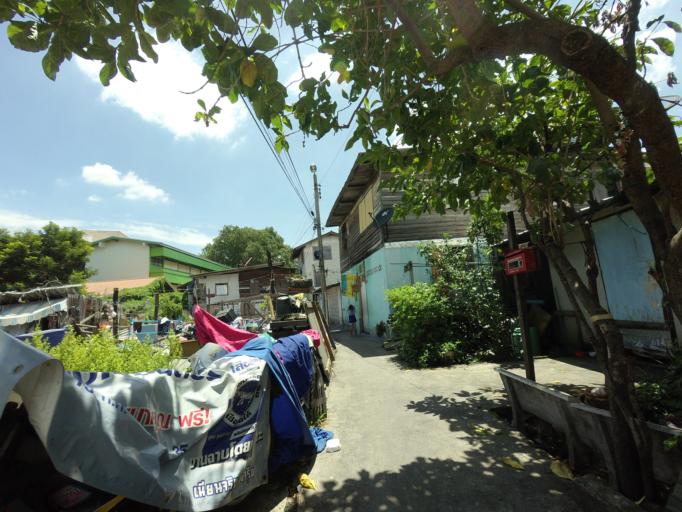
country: TH
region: Bangkok
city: Lat Phrao
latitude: 13.8041
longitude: 100.5884
